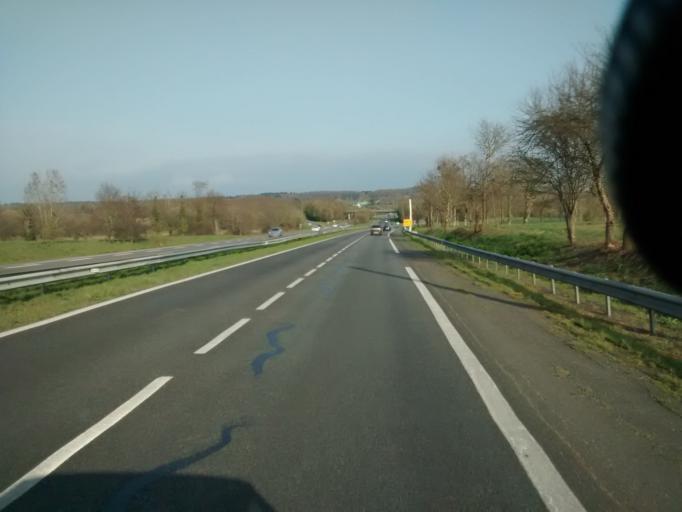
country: FR
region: Brittany
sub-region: Departement d'Ille-et-Vilaine
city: Montauban-de-Bretagne
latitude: 48.2076
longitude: -2.0529
